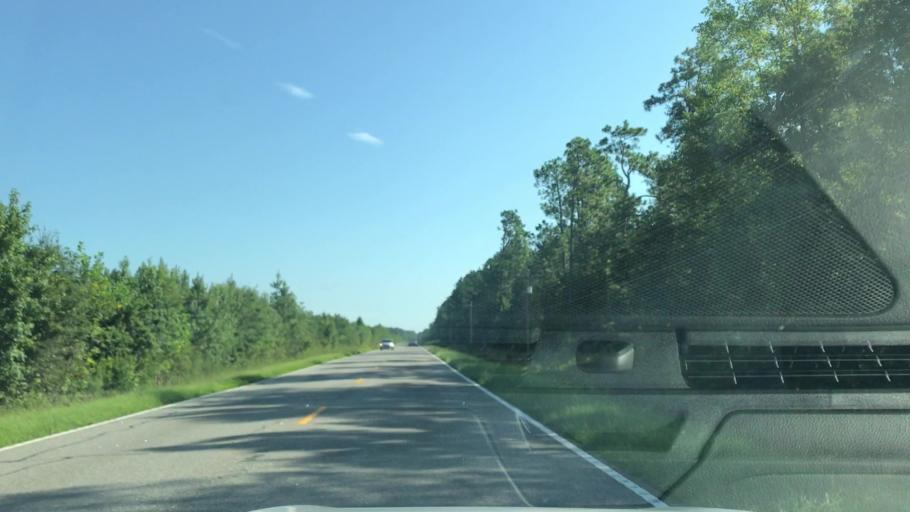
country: US
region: South Carolina
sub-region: Georgetown County
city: Georgetown
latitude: 33.5101
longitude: -79.2523
